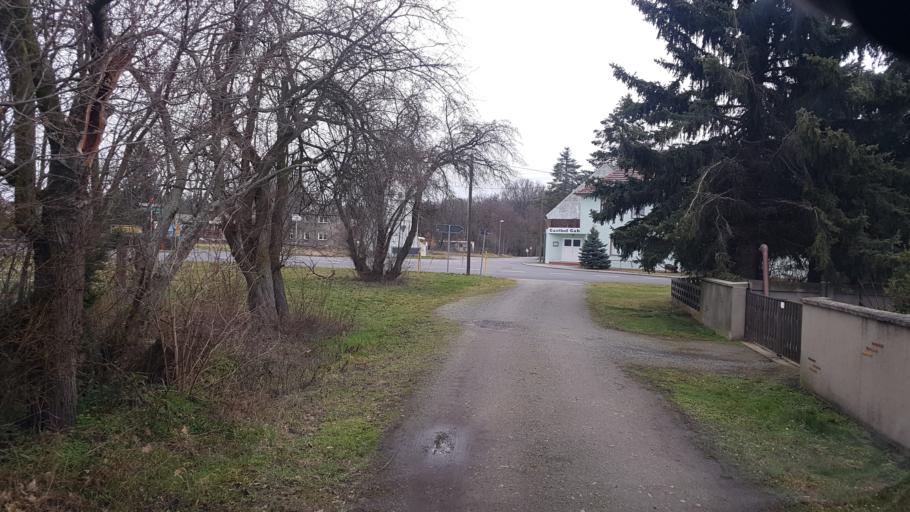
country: DE
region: Brandenburg
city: Crinitz
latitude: 51.7382
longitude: 13.7196
